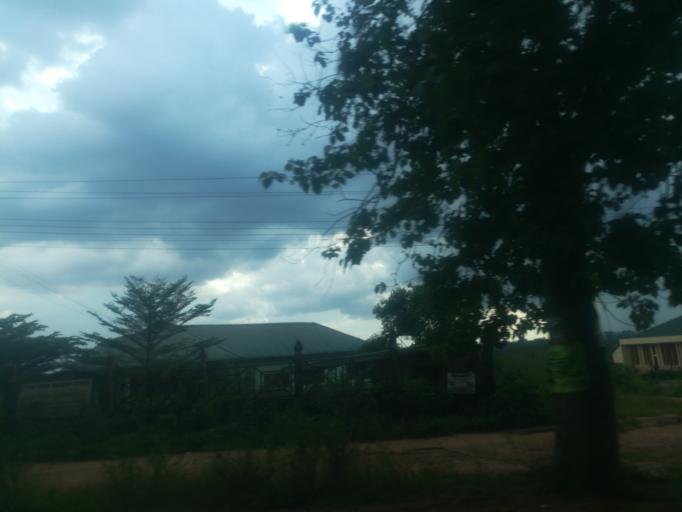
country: NG
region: Oyo
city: Ibadan
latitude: 7.4338
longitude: 3.8889
